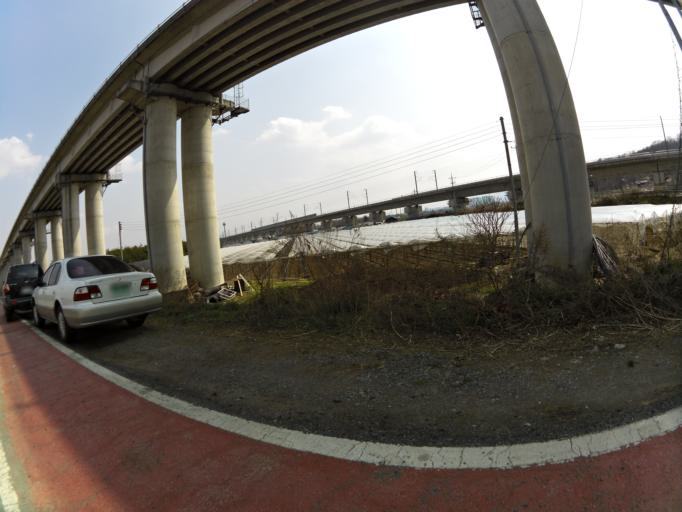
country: KR
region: Gyeongsangbuk-do
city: Gyeongsan-si
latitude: 35.8550
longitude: 128.7187
